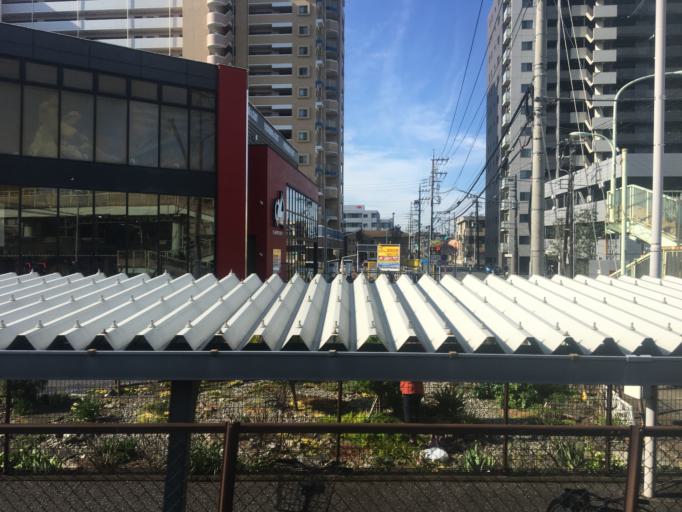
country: JP
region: Saitama
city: Sakado
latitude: 35.9480
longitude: 139.4099
